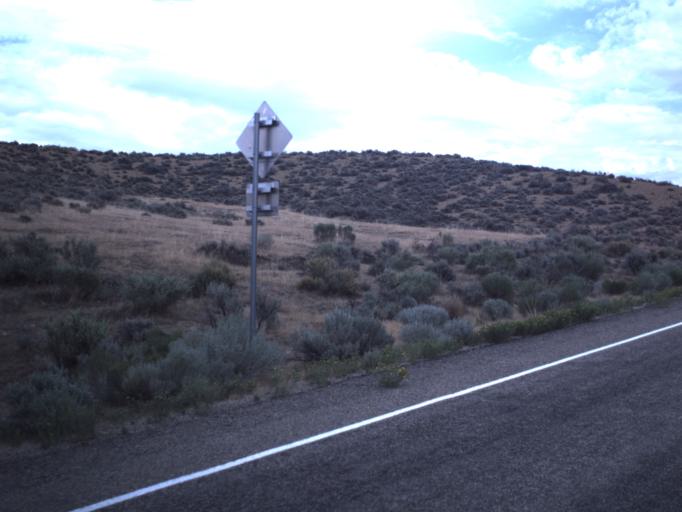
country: US
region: Colorado
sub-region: Rio Blanco County
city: Rangely
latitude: 39.9632
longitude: -109.1631
